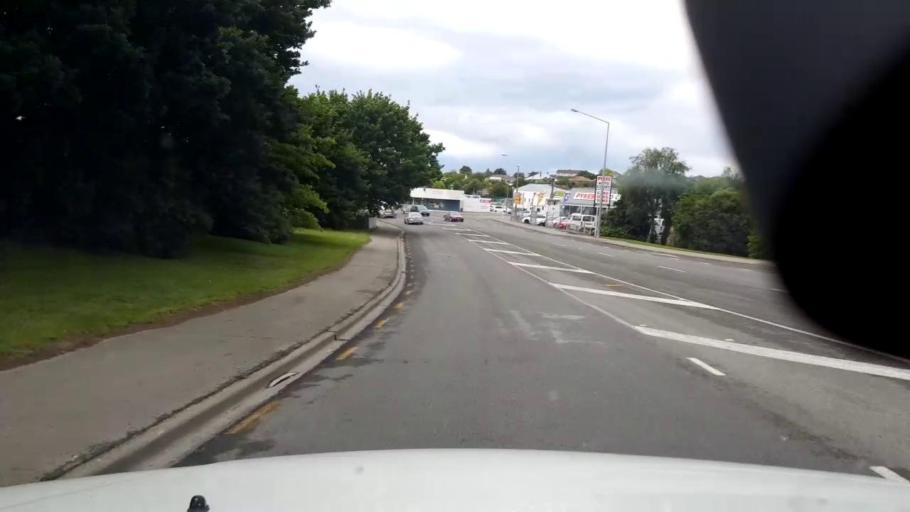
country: NZ
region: Canterbury
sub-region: Timaru District
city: Timaru
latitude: -44.3726
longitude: 171.2415
